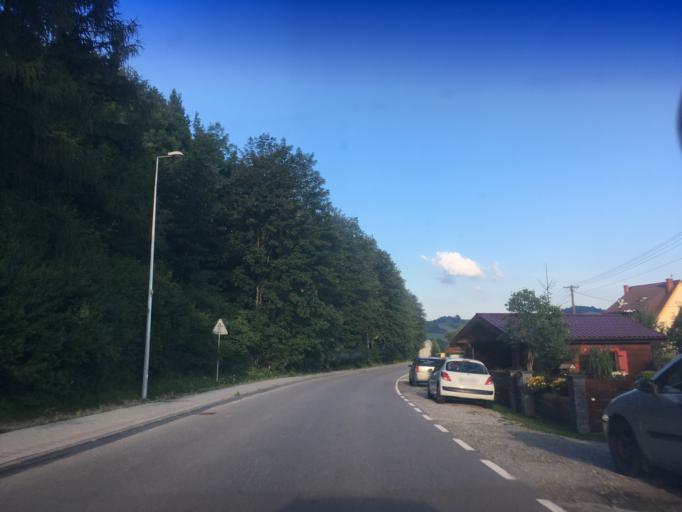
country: PL
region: Lesser Poland Voivodeship
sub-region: Powiat nowotarski
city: Kroscienko nad Dunajcem
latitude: 49.3941
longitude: 20.3898
